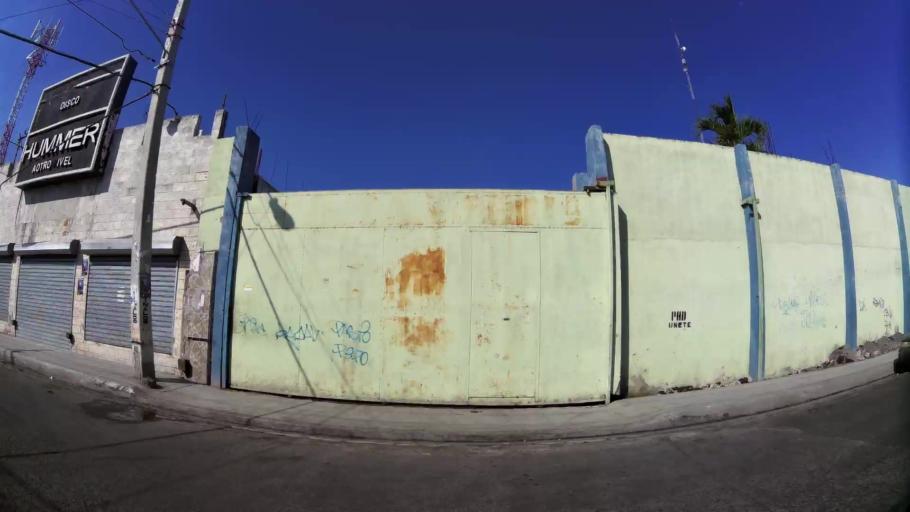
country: DO
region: Nacional
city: Santo Domingo
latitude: 18.4776
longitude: -69.9758
